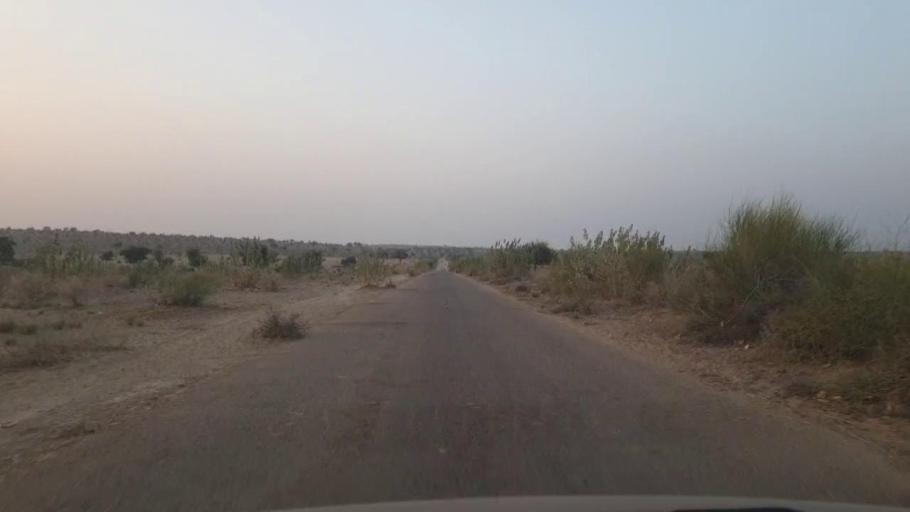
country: PK
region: Sindh
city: Umarkot
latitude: 25.2999
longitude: 70.0737
